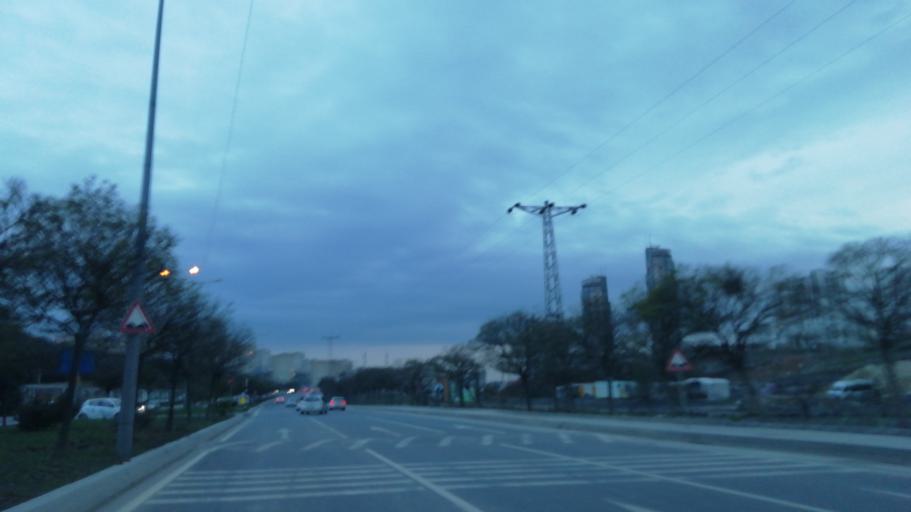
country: TR
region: Istanbul
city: Mahmutbey
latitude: 41.0474
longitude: 28.7740
